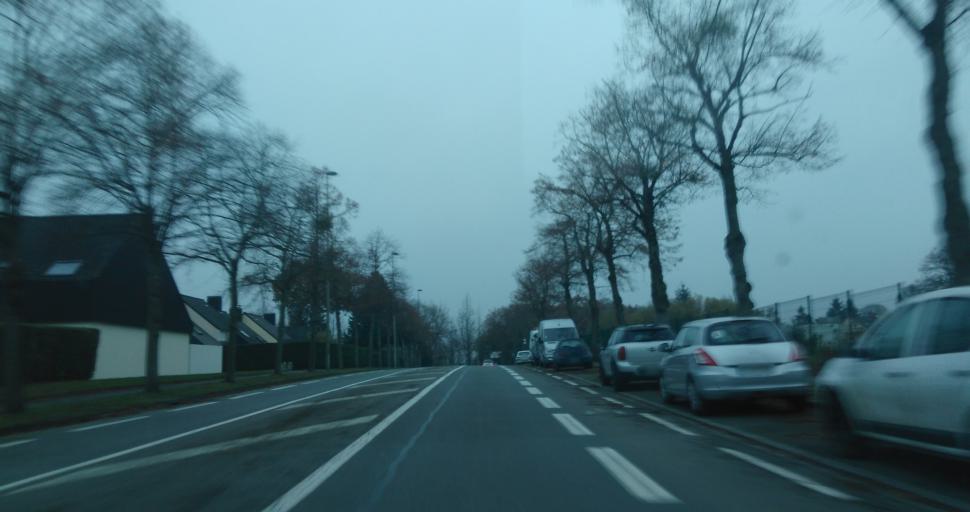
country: FR
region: Brittany
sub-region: Departement d'Ille-et-Vilaine
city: Rennes
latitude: 48.1281
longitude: -1.6421
